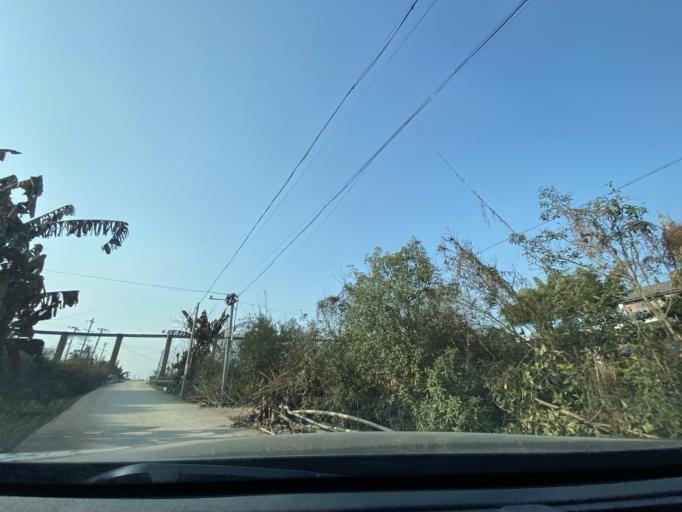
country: CN
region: Sichuan
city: Wenlin
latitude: 30.2518
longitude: 104.2537
